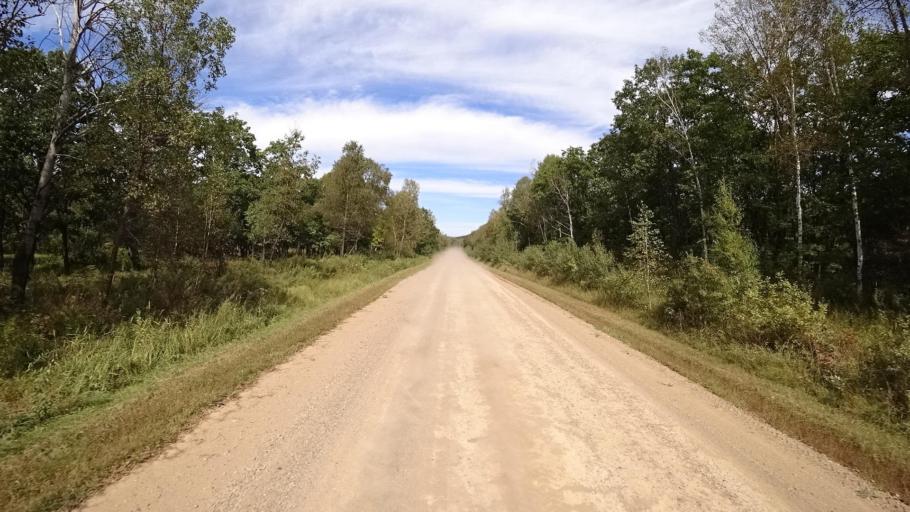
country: RU
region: Primorskiy
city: Yakovlevka
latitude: 44.6900
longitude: 133.6186
